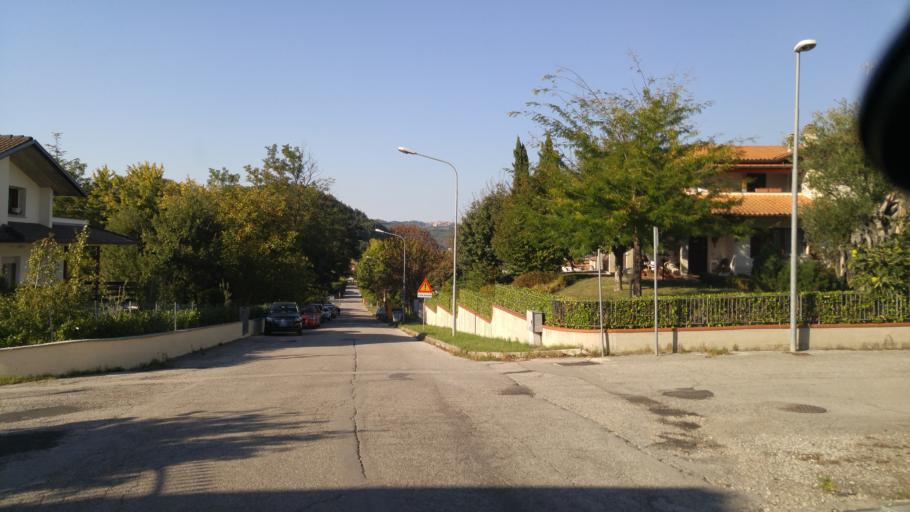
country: IT
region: The Marches
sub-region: Provincia di Pesaro e Urbino
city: Fermignano
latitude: 43.6667
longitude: 12.6449
